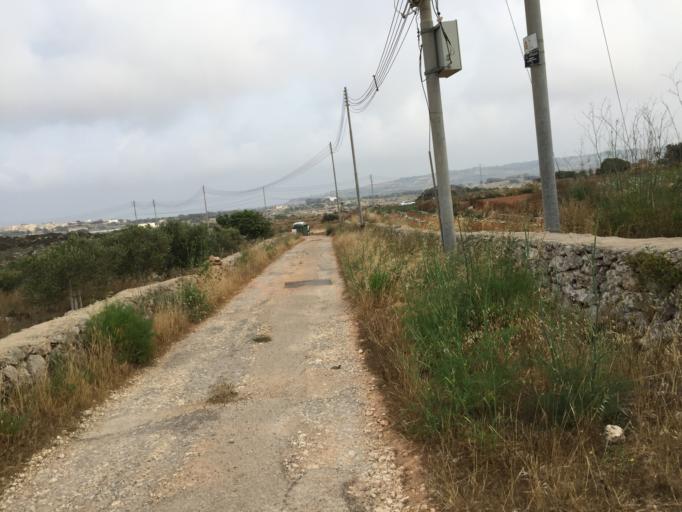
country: MT
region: L-Imgarr
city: Imgarr
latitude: 35.9333
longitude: 14.3861
